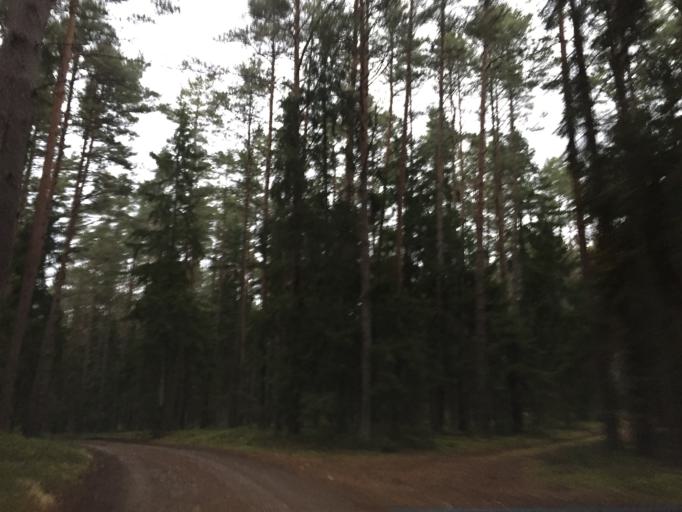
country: EE
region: Saare
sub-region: Kuressaare linn
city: Kuressaare
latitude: 58.5889
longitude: 22.5112
